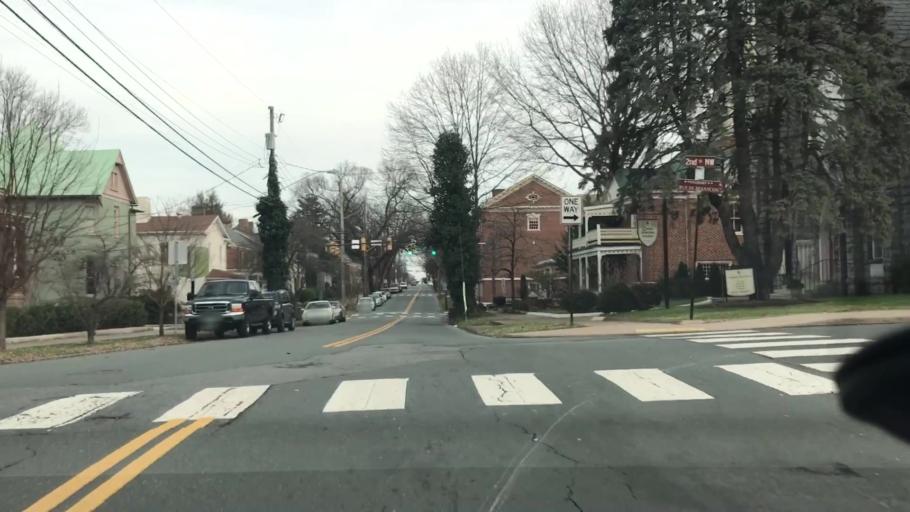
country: US
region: Virginia
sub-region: City of Charlottesville
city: Charlottesville
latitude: 38.0332
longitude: -78.4814
